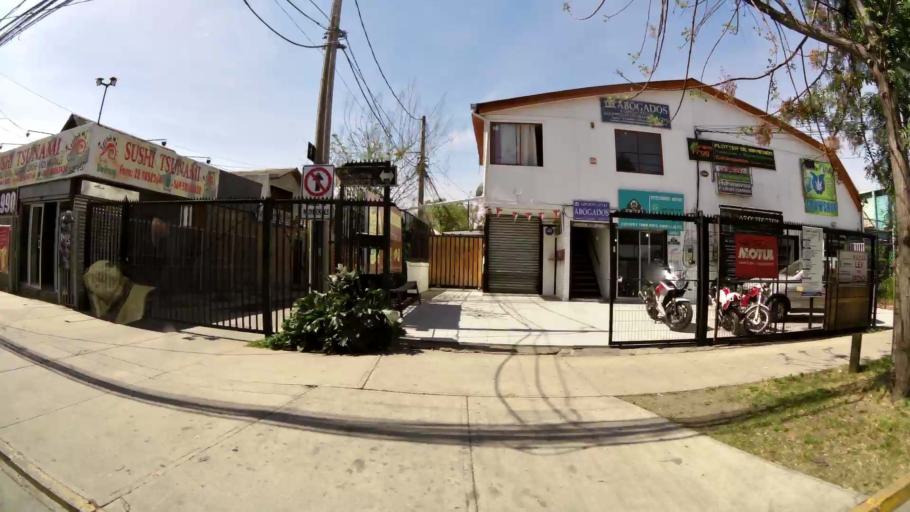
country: CL
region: Santiago Metropolitan
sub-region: Provincia de Cordillera
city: Puente Alto
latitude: -33.5937
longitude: -70.5788
